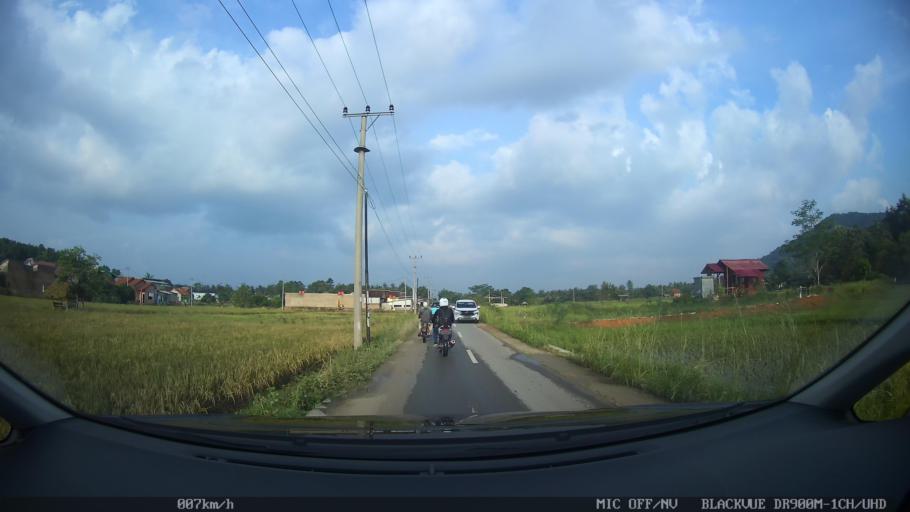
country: ID
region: Lampung
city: Kedaton
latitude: -5.3921
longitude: 105.3262
